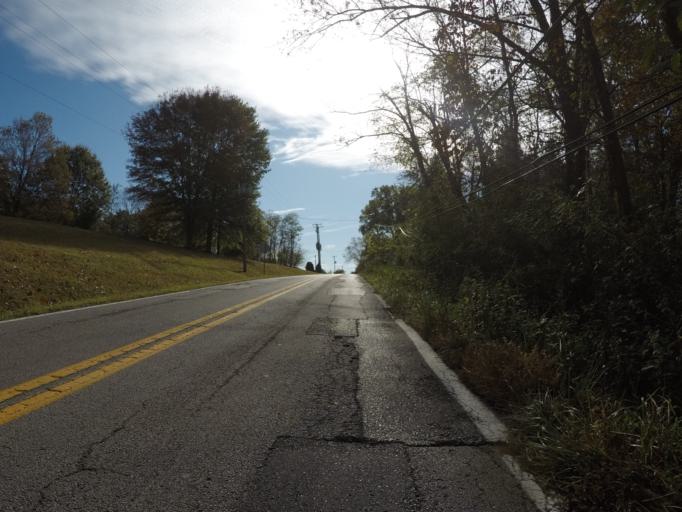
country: US
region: West Virginia
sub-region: Wayne County
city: Ceredo
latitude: 38.3615
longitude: -82.5288
